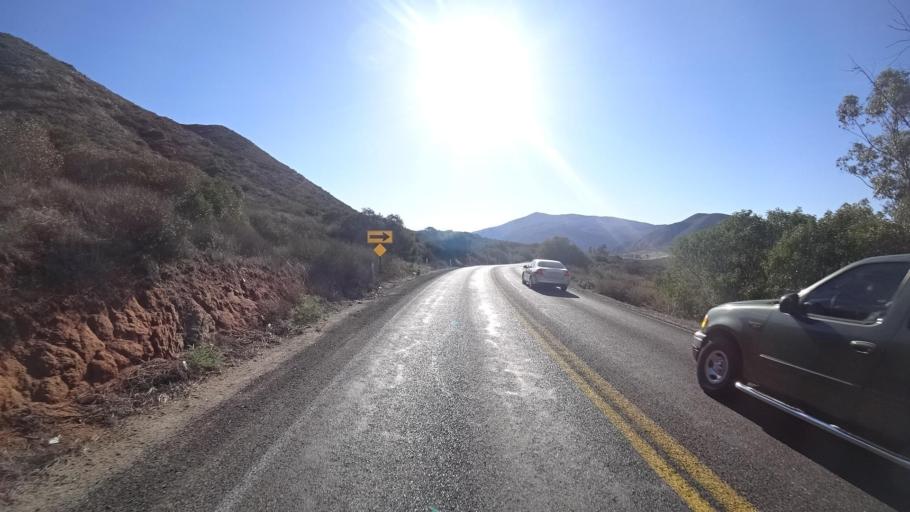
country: MX
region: Baja California
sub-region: Tijuana
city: Villa del Campo
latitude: 32.6206
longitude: -116.7436
